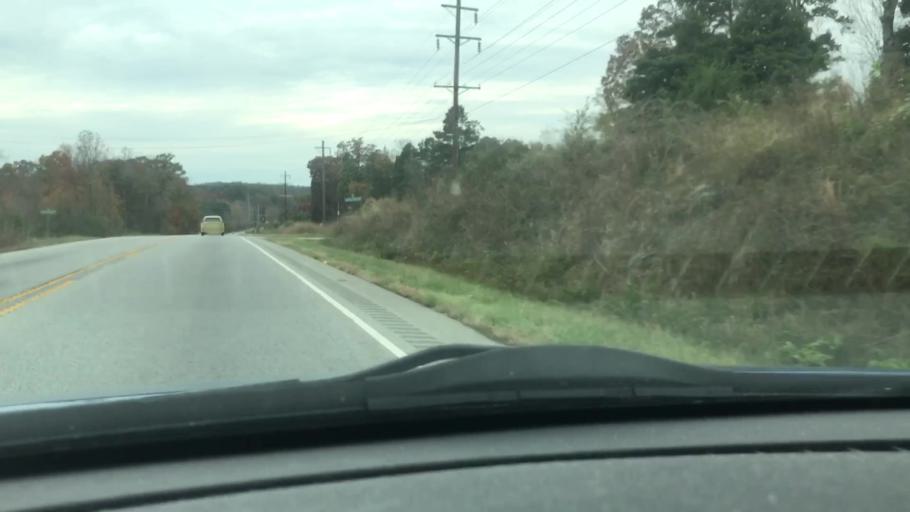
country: US
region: North Carolina
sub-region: Davidson County
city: Thomasville
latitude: 35.7525
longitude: -80.0303
